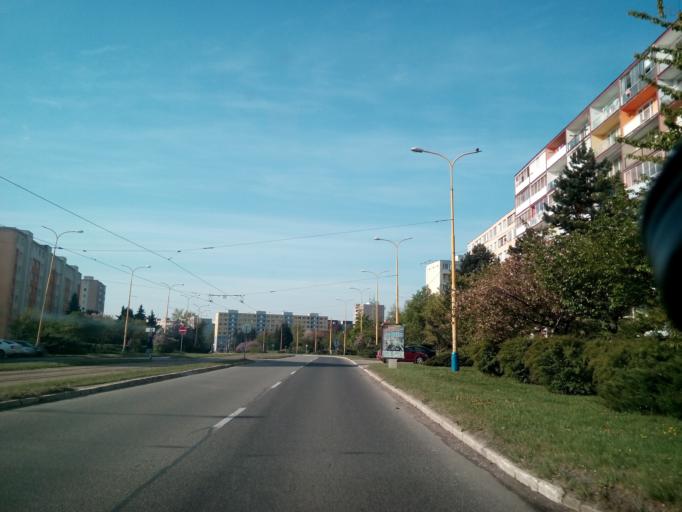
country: SK
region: Kosicky
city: Kosice
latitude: 48.7214
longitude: 21.2345
